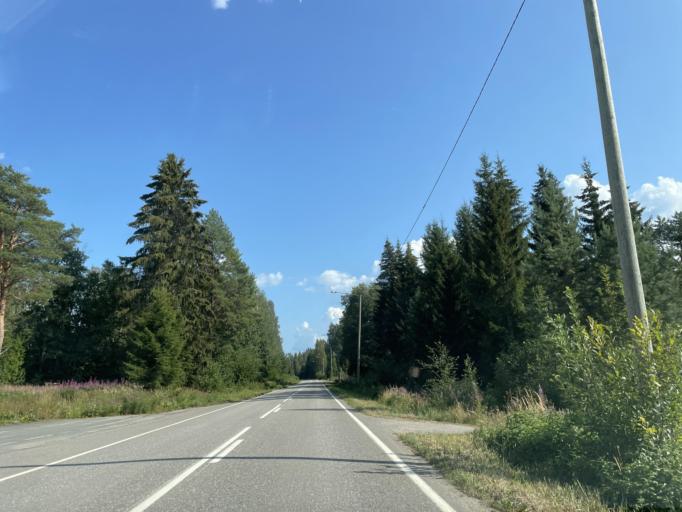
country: FI
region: Central Finland
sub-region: Saarijaervi-Viitasaari
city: Pihtipudas
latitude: 63.3579
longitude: 25.7526
